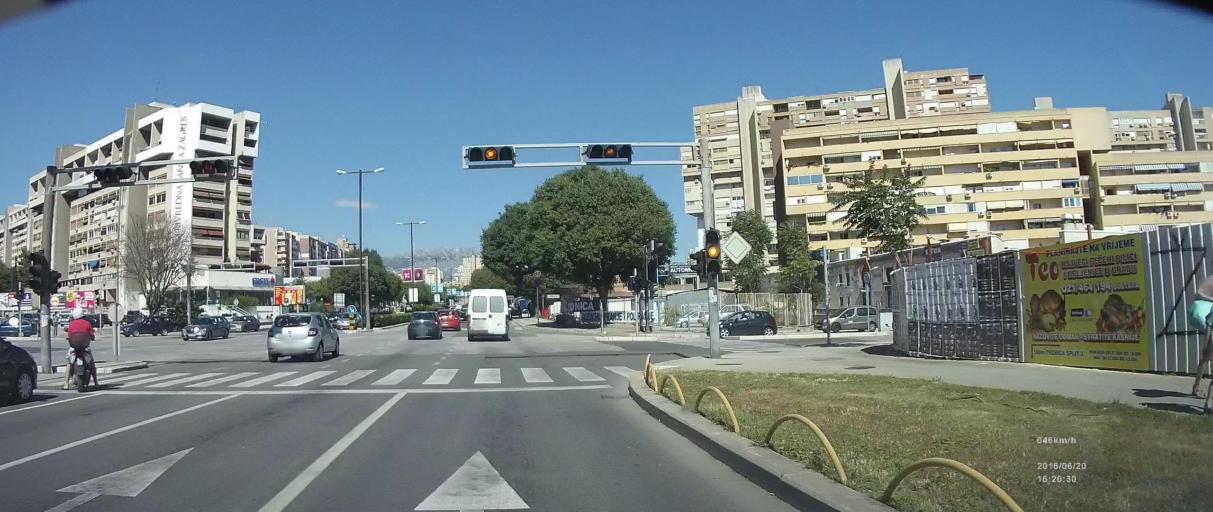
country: HR
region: Splitsko-Dalmatinska
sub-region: Grad Split
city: Split
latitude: 43.5064
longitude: 16.4641
